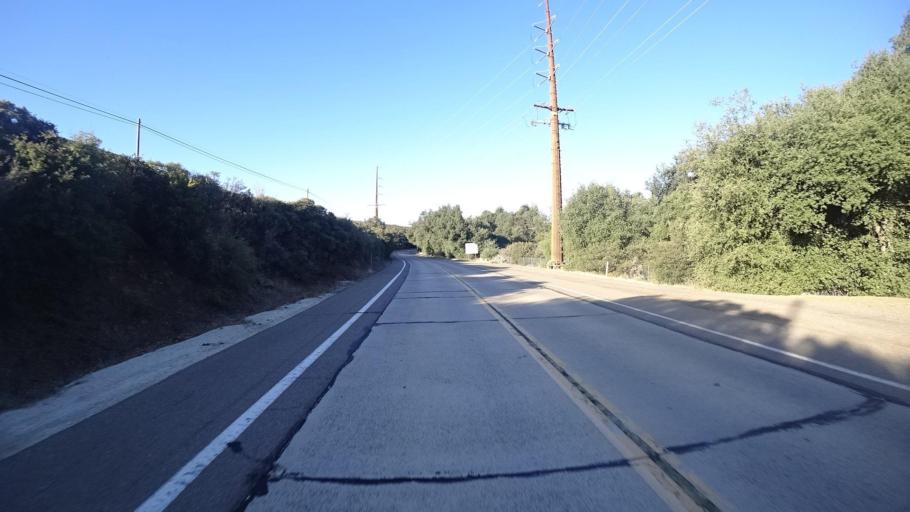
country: US
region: California
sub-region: San Diego County
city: Descanso
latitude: 32.8554
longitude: -116.5892
